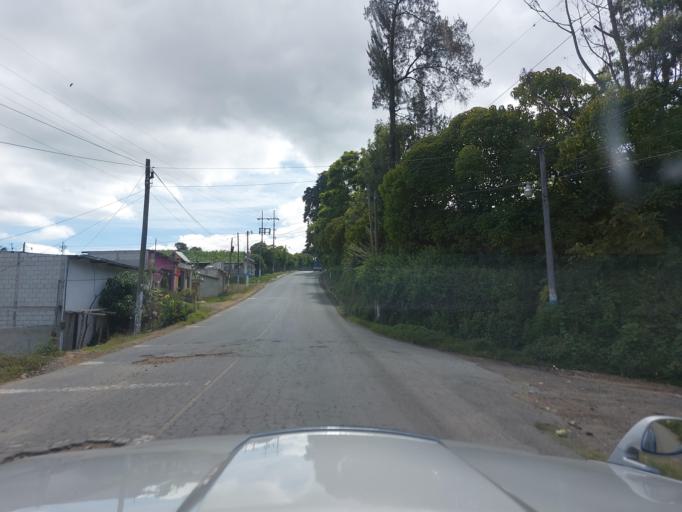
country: GT
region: Chimaltenango
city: Parramos
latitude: 14.6086
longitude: -90.8086
